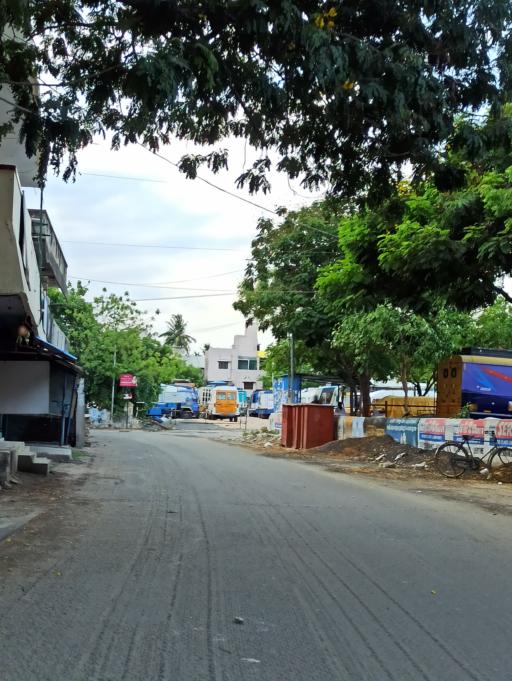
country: IN
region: Tamil Nadu
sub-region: Chennai
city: Chetput
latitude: 13.0554
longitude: 80.2079
